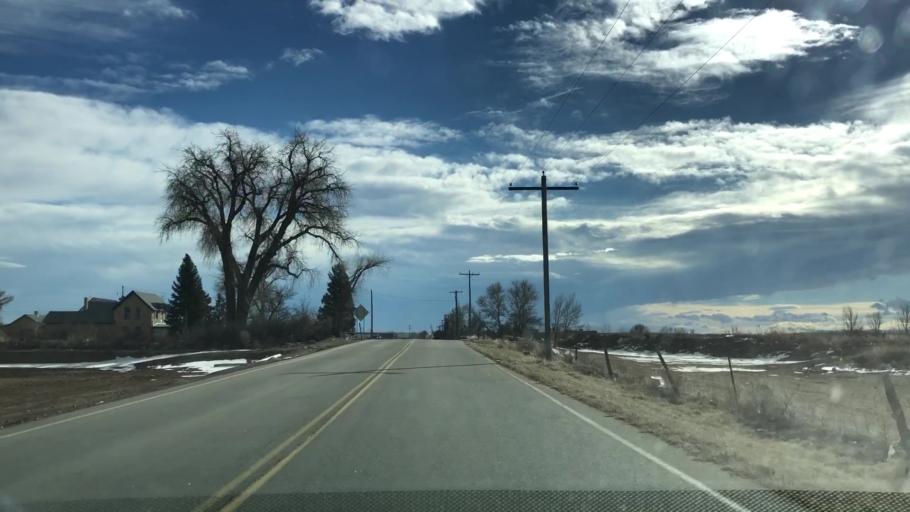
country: US
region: Colorado
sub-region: Weld County
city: Windsor
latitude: 40.5108
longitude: -104.9442
